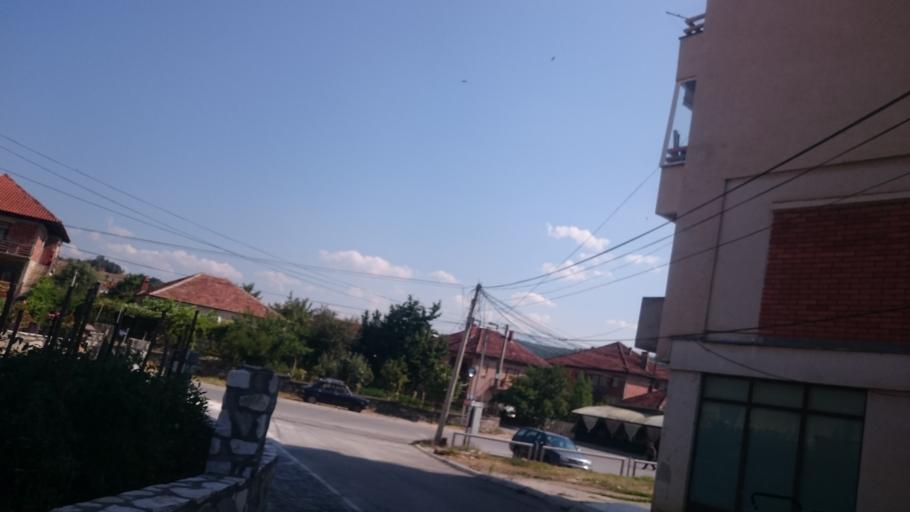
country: MK
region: Makedonski Brod
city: Makedonski Brod
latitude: 41.5131
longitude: 21.2160
